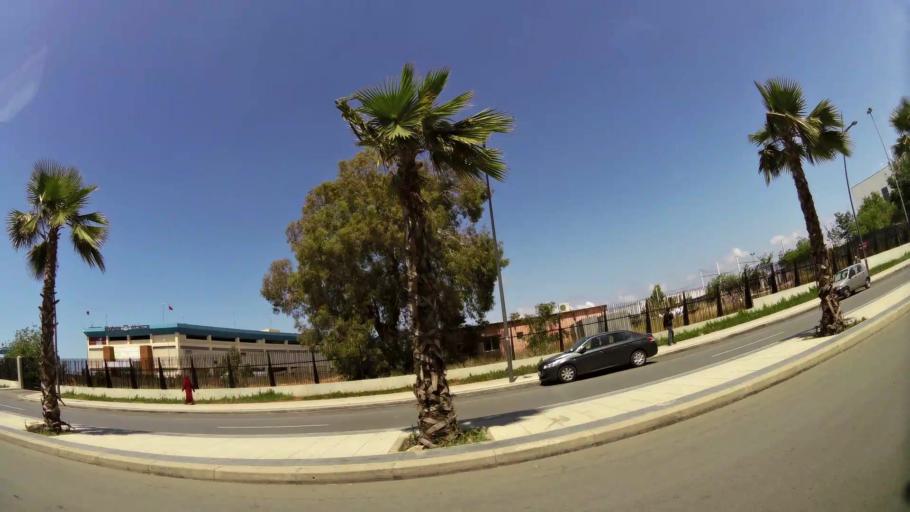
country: MA
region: Rabat-Sale-Zemmour-Zaer
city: Sale
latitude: 34.0503
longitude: -6.7966
